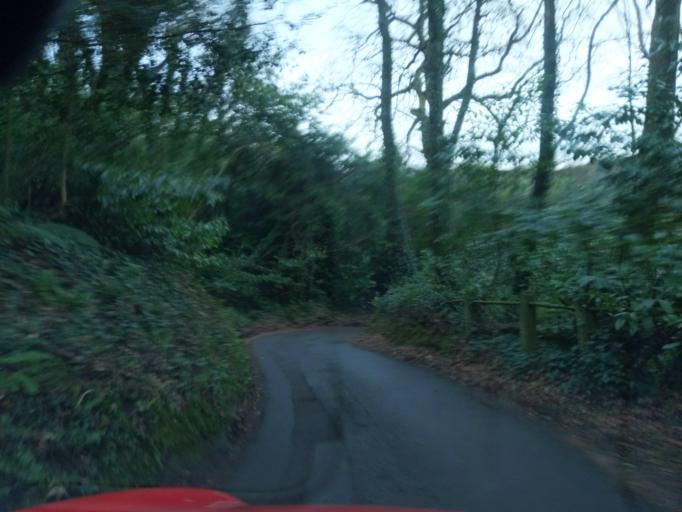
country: GB
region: England
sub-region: Devon
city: Wembury
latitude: 50.3270
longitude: -4.0797
